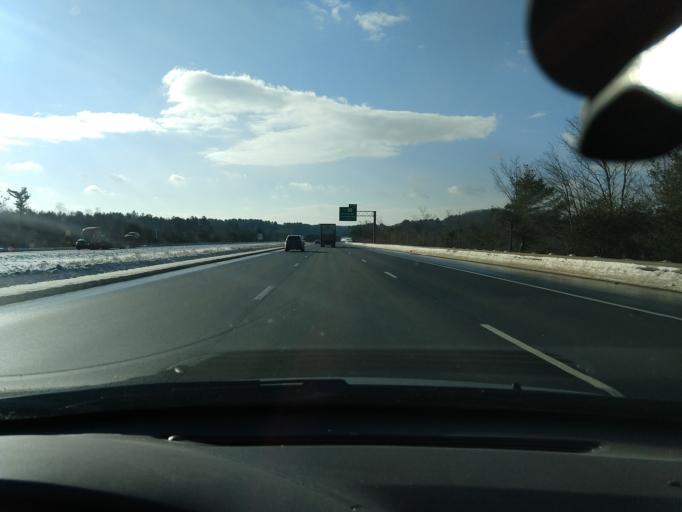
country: US
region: Massachusetts
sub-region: Worcester County
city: Sturbridge
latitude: 42.1020
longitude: -72.0853
